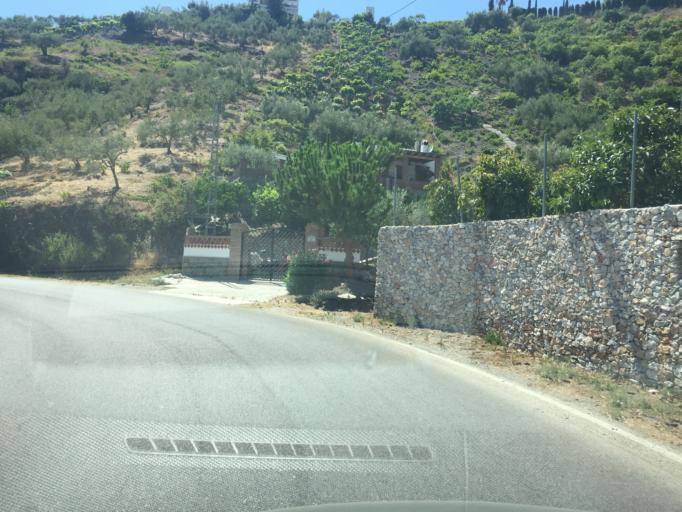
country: ES
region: Andalusia
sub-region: Provincia de Malaga
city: Frigiliana
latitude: 36.8053
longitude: -3.9168
